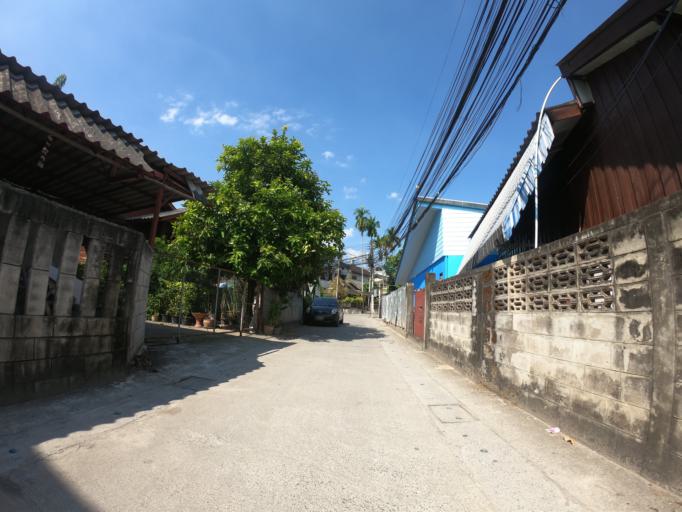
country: TH
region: Chiang Mai
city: Chiang Mai
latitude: 18.7979
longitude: 98.9880
